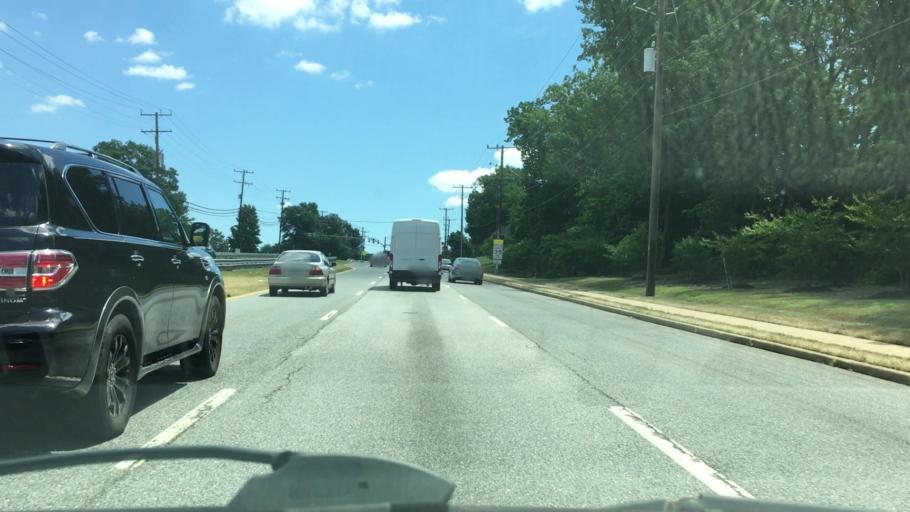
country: US
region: Maryland
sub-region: Prince George's County
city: Greenbelt
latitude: 38.9933
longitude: -76.8714
